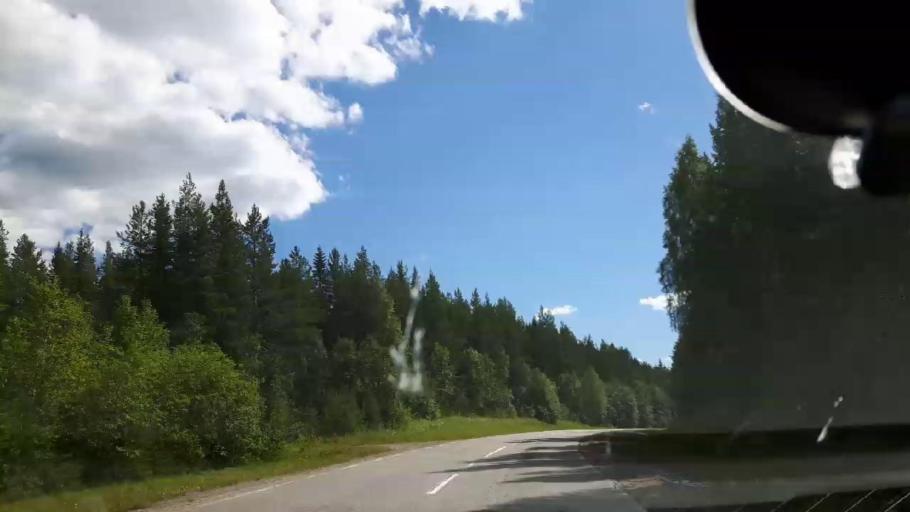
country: SE
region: Vaesternorrland
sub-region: Ange Kommun
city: Fransta
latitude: 62.8122
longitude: 16.2115
